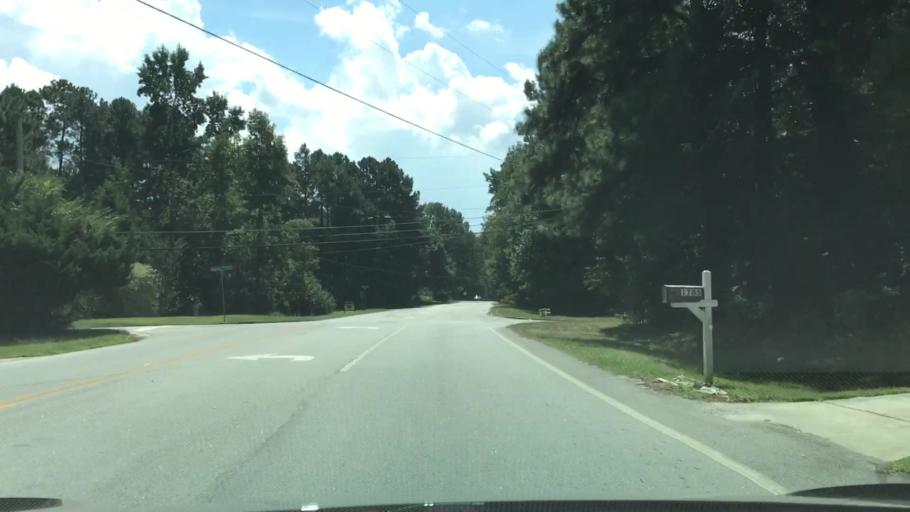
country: US
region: Georgia
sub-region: Gwinnett County
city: Snellville
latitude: 33.8617
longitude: -84.0490
